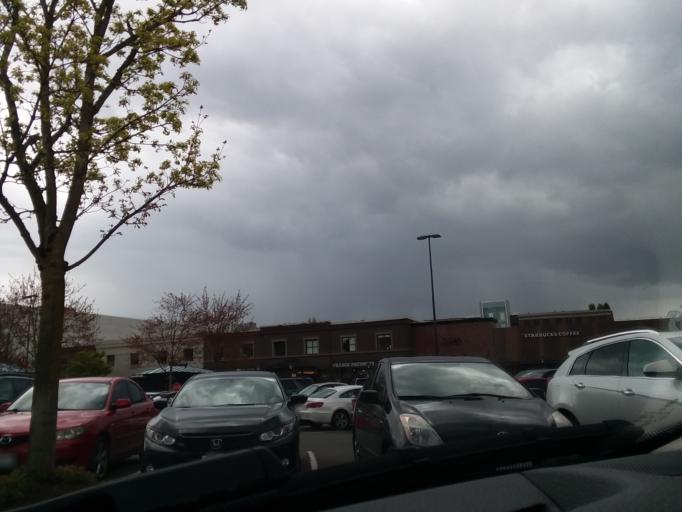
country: US
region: Washington
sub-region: King County
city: Seattle
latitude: 47.6632
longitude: -122.2998
